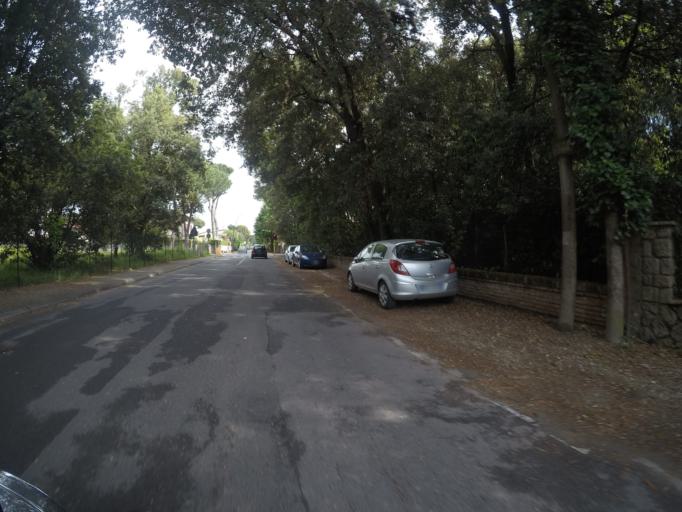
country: IT
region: Tuscany
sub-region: Provincia di Massa-Carrara
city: Capanne-Prato-Cinquale
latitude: 43.9737
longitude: 10.1519
